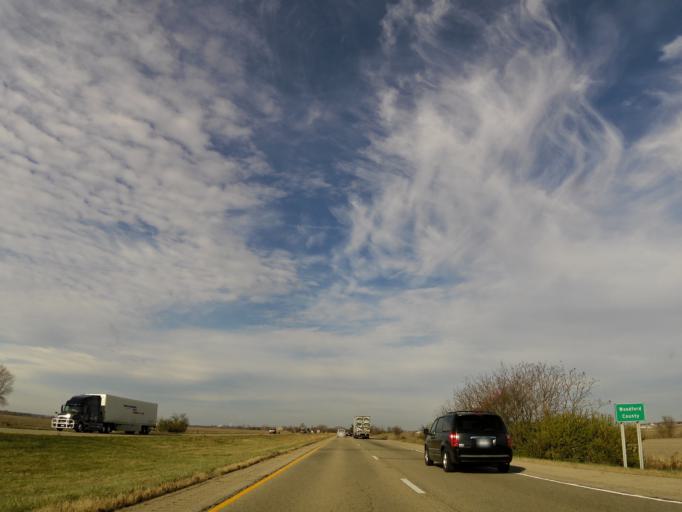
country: US
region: Illinois
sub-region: McLean County
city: Danvers
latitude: 40.5962
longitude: -89.1592
